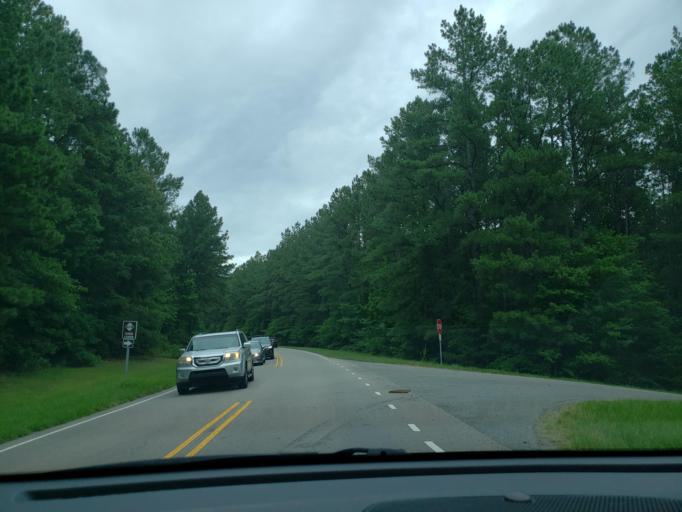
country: US
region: North Carolina
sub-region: Orange County
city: Chapel Hill
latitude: 35.8679
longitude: -79.0010
